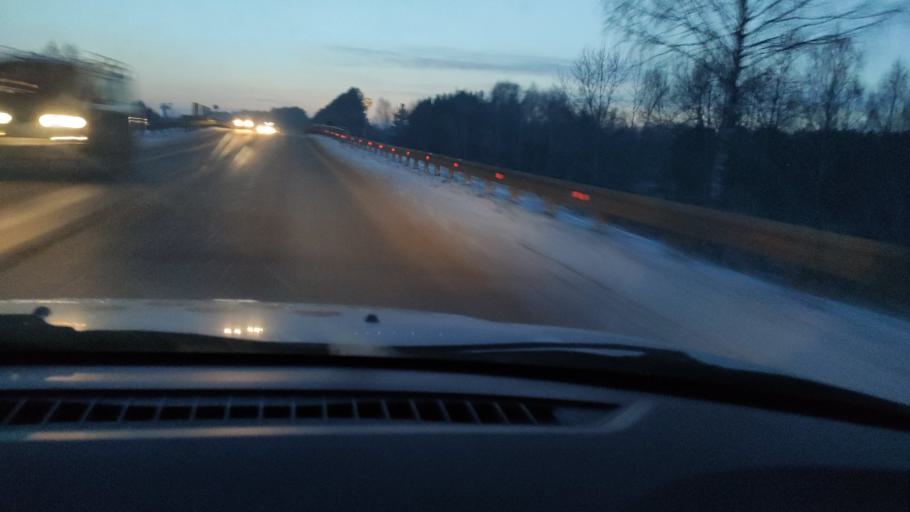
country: RU
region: Perm
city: Kungur
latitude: 57.4222
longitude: 56.9247
